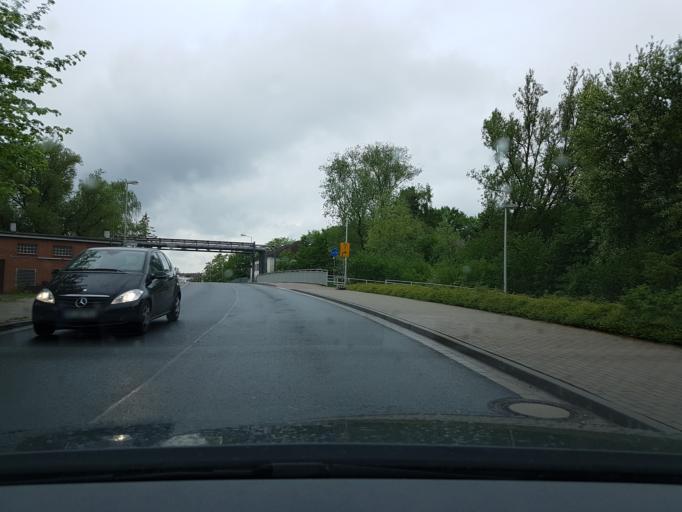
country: DE
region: Lower Saxony
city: Hameln
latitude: 52.0934
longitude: 9.3748
